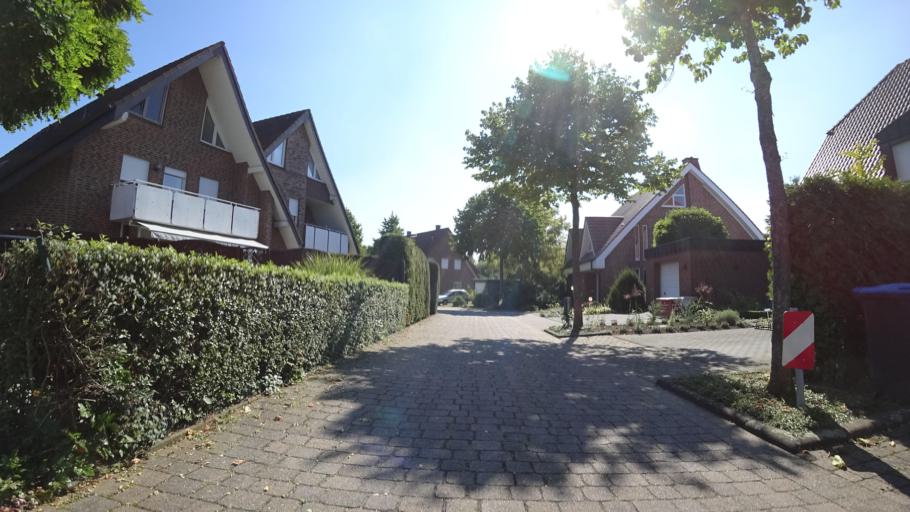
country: DE
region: North Rhine-Westphalia
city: Oelde
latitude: 51.8310
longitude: 8.1417
